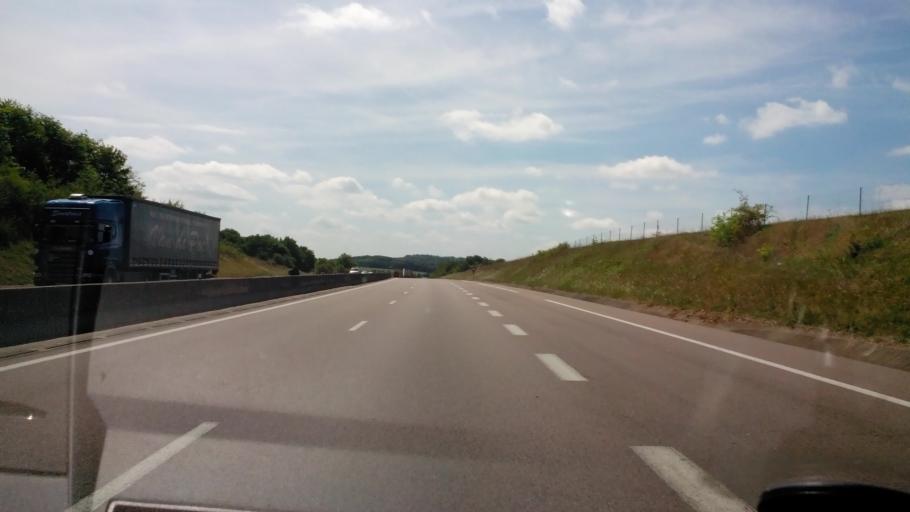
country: FR
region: Lorraine
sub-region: Departement de Meurthe-et-Moselle
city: Colombey-les-Belles
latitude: 48.4238
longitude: 5.8604
